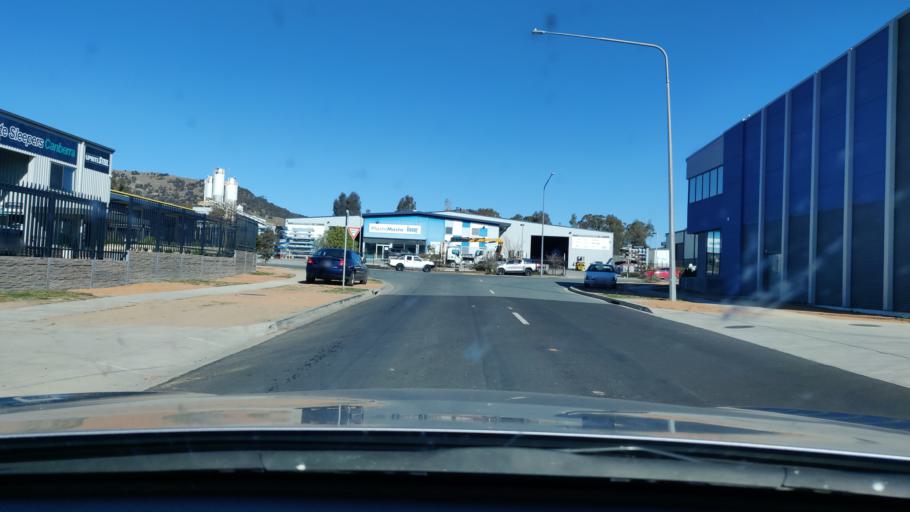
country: AU
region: Australian Capital Territory
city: Macarthur
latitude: -35.3983
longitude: 149.1584
